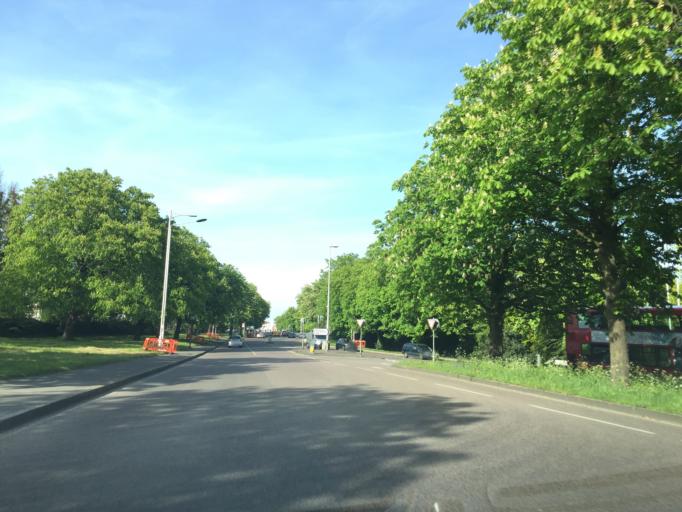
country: GB
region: England
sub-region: Greater London
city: Woodford Green
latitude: 51.6054
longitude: 0.0181
